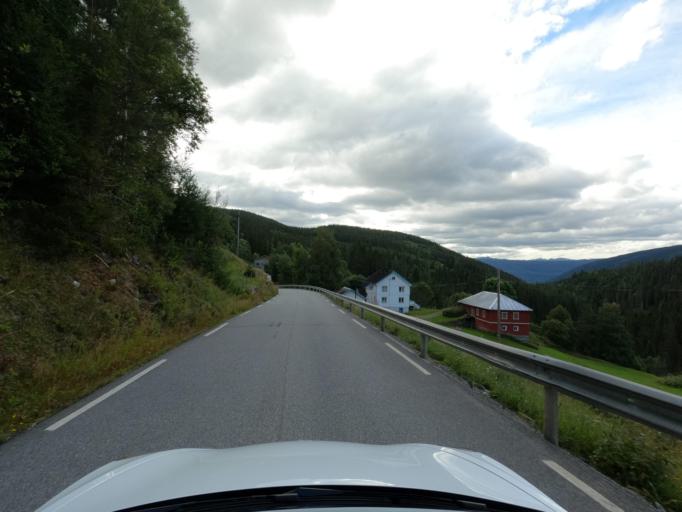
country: NO
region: Telemark
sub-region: Tinn
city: Rjukan
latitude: 60.0579
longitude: 8.7335
